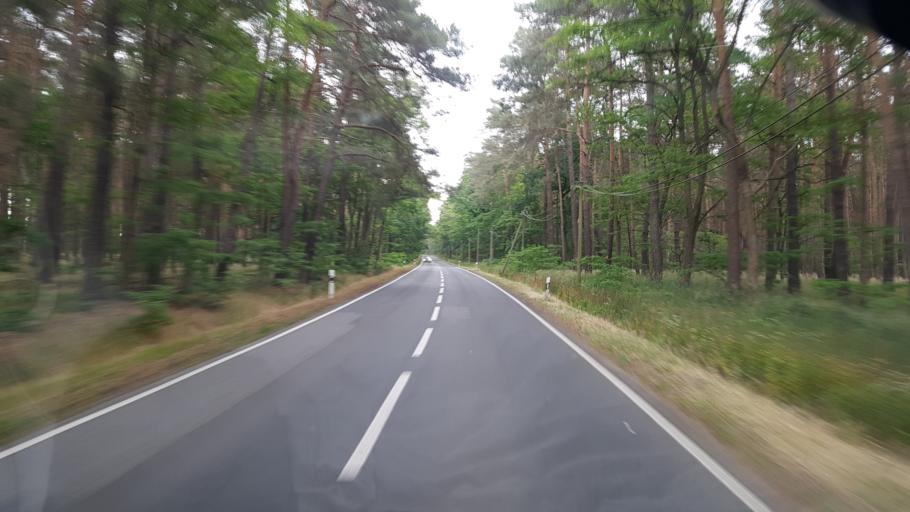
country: DE
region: Brandenburg
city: Ihlow
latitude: 51.8121
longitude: 13.2520
